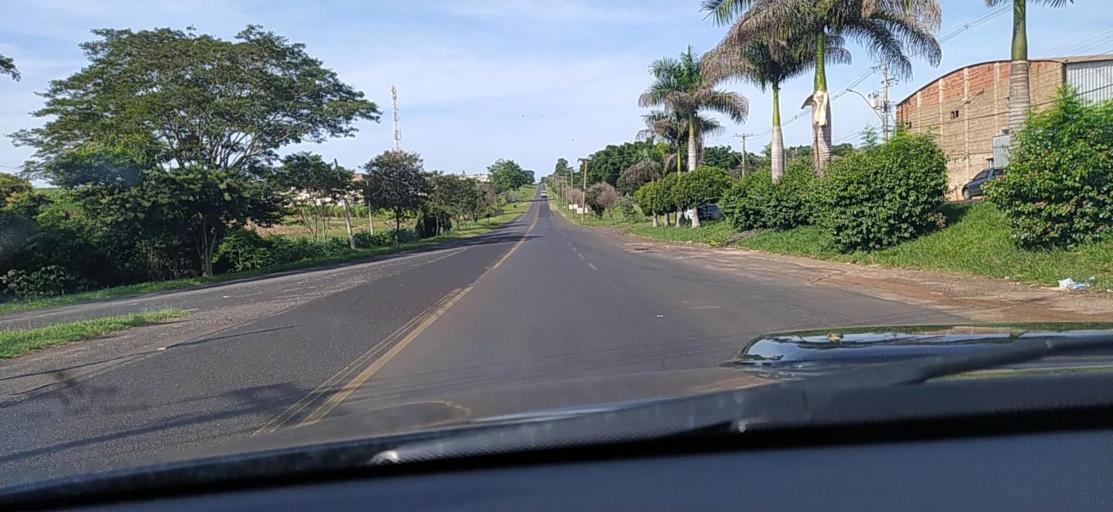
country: BR
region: Sao Paulo
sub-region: Pindorama
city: Pindorama
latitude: -21.1926
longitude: -48.9142
